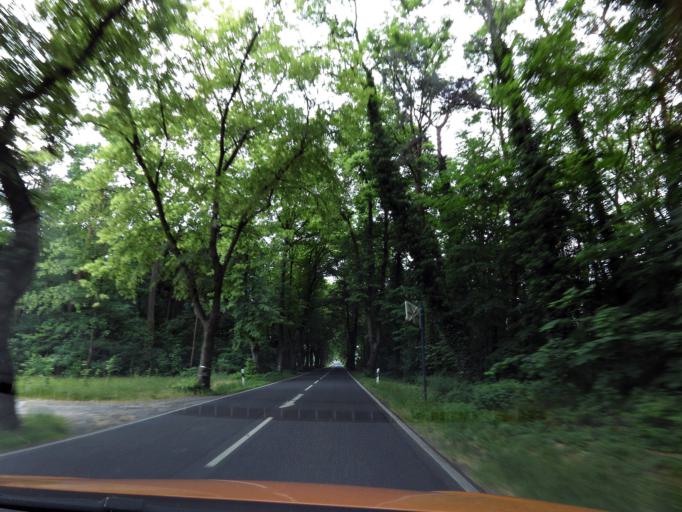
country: DE
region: Brandenburg
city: Rangsdorf
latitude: 52.2680
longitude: 13.3606
